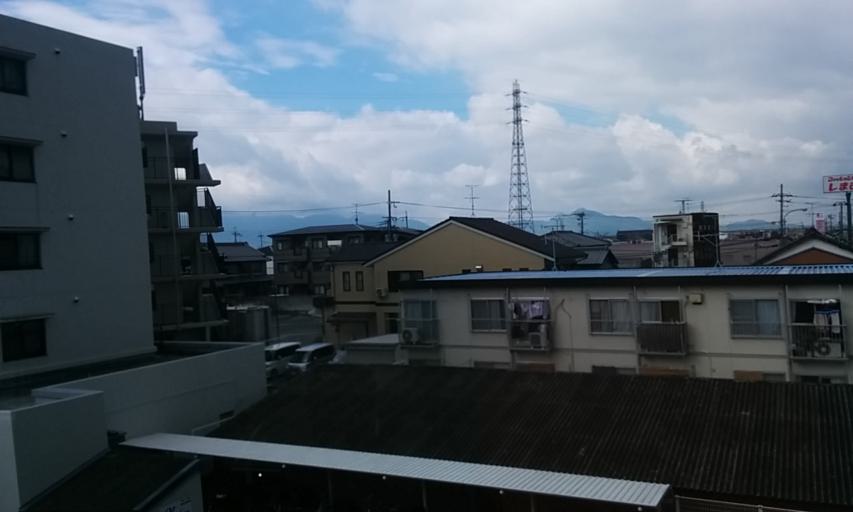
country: JP
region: Nara
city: Tawaramoto
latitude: 34.5503
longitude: 135.7917
